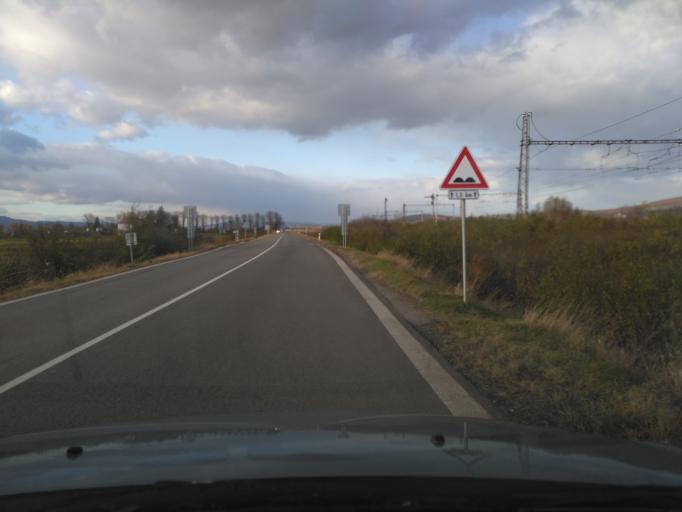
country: HU
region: Borsod-Abauj-Zemplen
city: Satoraljaujhely
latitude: 48.4119
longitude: 21.6659
